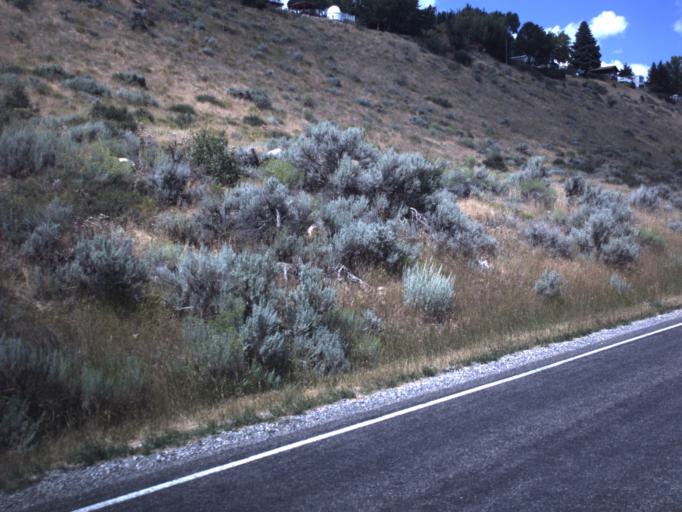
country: US
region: Utah
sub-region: Rich County
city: Randolph
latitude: 41.8918
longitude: -111.3664
